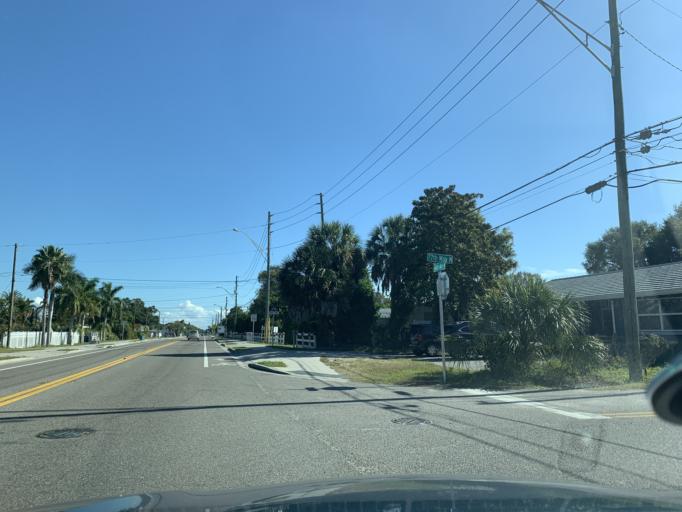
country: US
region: Florida
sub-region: Pinellas County
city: Kenneth City
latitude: 27.8136
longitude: -82.7451
